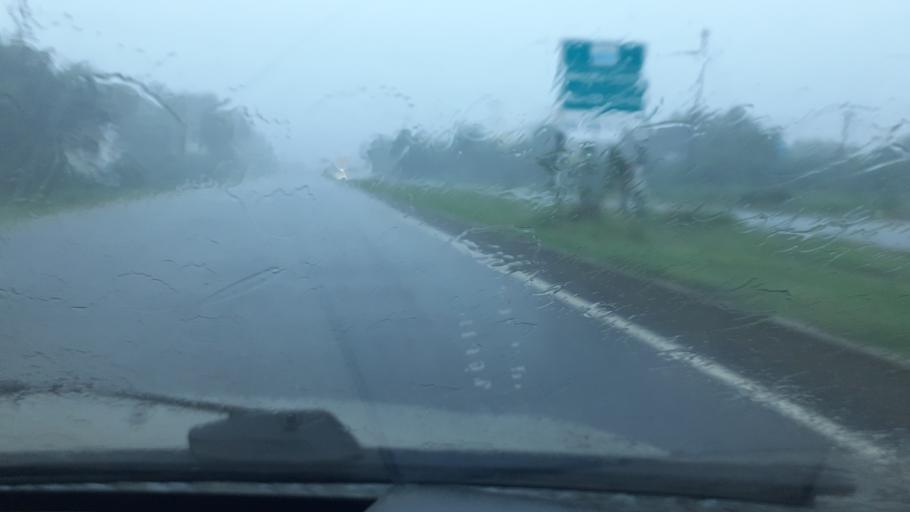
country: IN
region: Tamil Nadu
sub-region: Virudhunagar
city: Virudunagar
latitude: 9.4965
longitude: 77.9416
